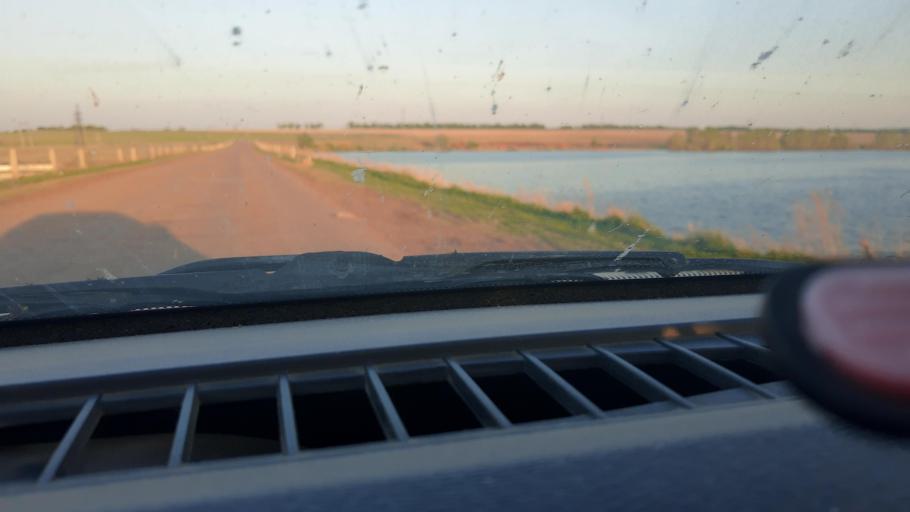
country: RU
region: Bashkortostan
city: Asanovo
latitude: 54.8522
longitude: 55.5873
